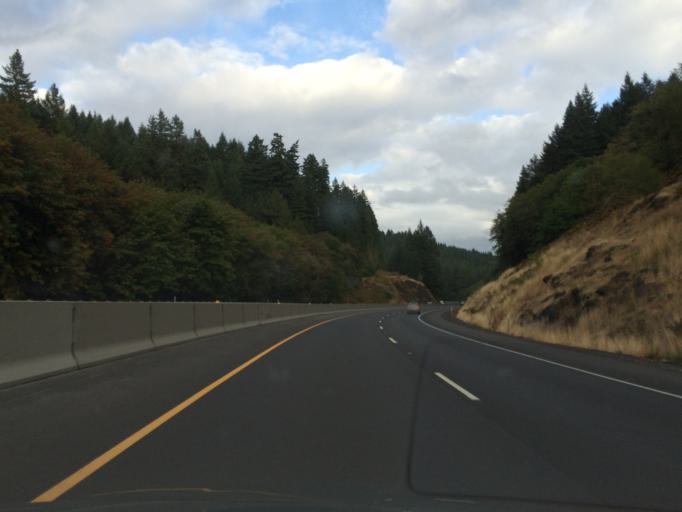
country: US
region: Oregon
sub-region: Lane County
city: Cottage Grove
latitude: 43.7527
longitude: -123.1538
